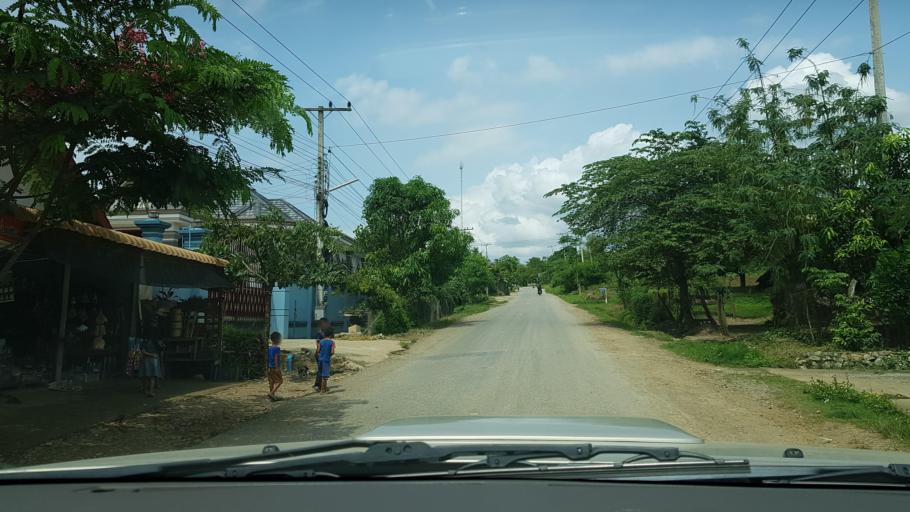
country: LA
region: Loungnamtha
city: Muang Nale
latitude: 20.0276
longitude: 101.3406
